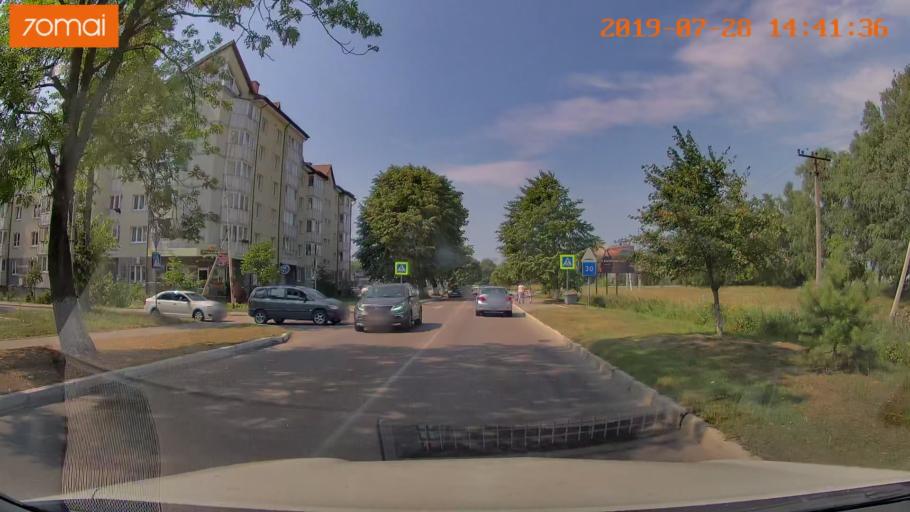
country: RU
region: Kaliningrad
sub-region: Gorod Kaliningrad
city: Yantarnyy
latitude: 54.8564
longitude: 19.9467
